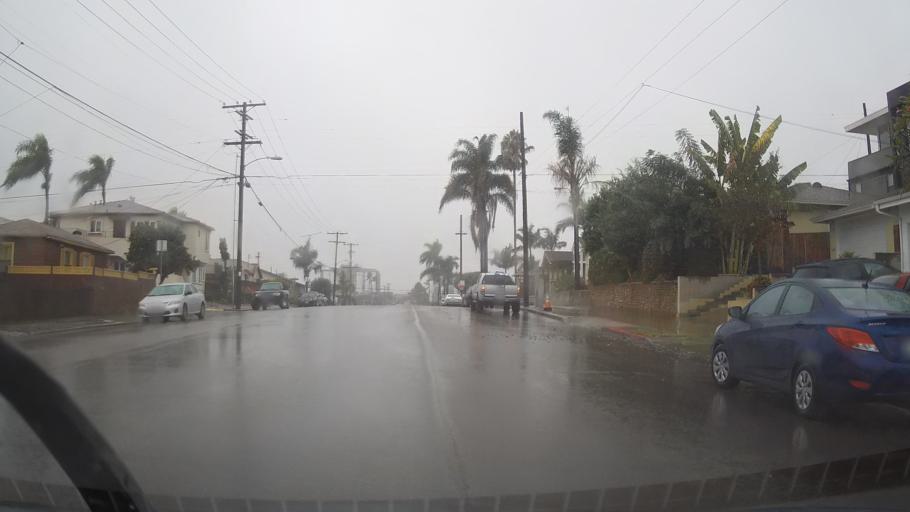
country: US
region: California
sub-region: San Diego County
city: San Diego
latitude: 32.7522
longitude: -117.1402
